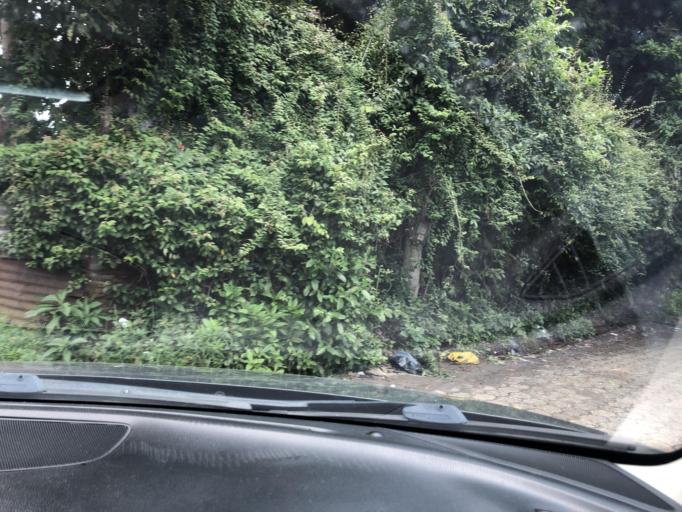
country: GT
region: Quetzaltenango
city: Coatepeque
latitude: 14.7076
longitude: -91.8657
